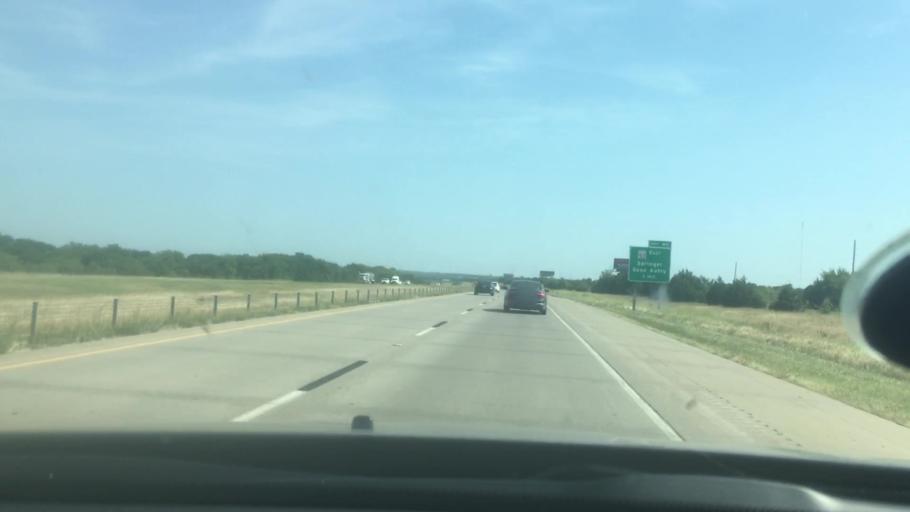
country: US
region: Oklahoma
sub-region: Carter County
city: Ardmore
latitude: 34.2848
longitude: -97.1596
